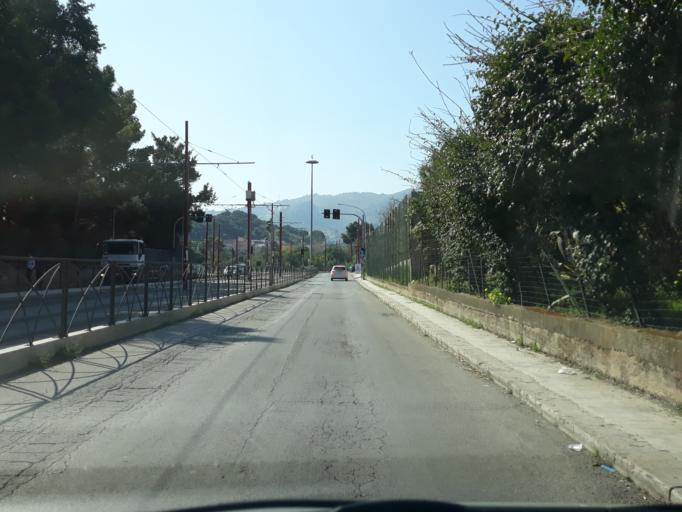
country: IT
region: Sicily
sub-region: Palermo
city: Palermo
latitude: 38.1275
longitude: 13.3026
